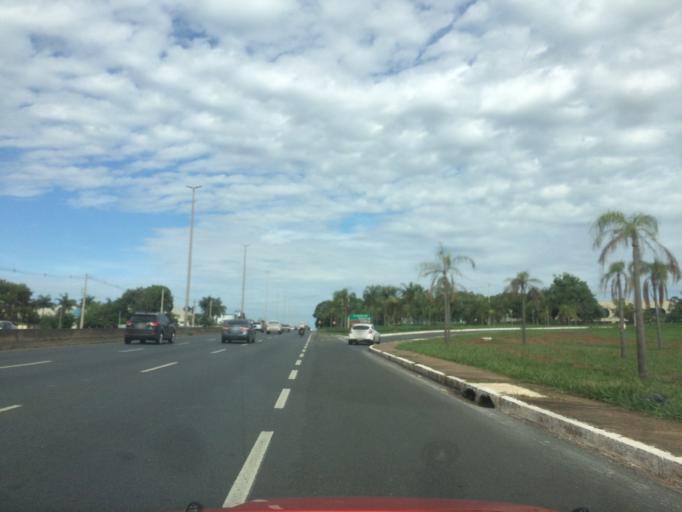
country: BR
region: Federal District
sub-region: Brasilia
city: Brasilia
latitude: -15.8166
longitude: -47.8360
